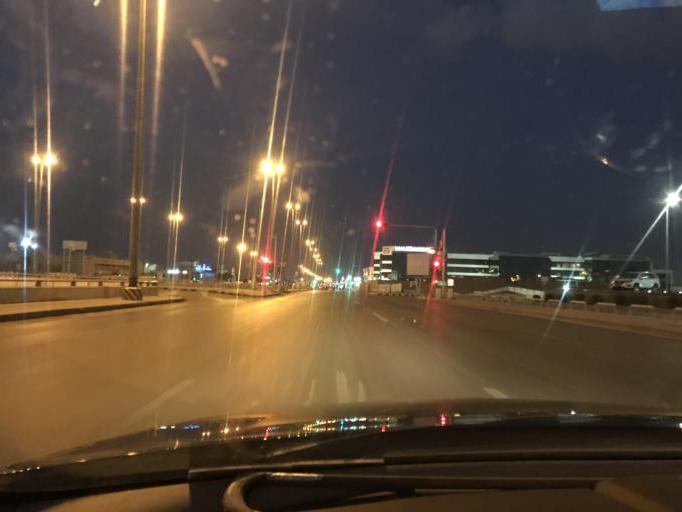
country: SA
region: Ar Riyad
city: Riyadh
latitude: 24.7203
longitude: 46.7722
